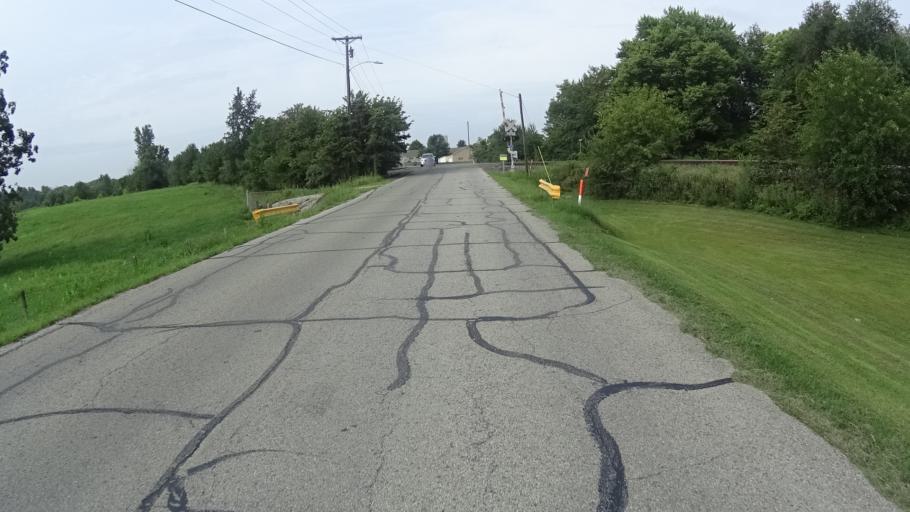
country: US
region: Indiana
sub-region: Madison County
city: Pendleton
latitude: 40.0227
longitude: -85.7366
